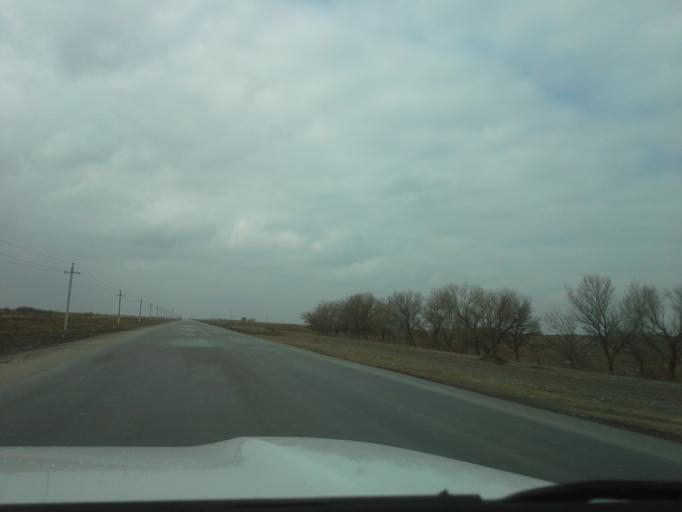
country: TM
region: Ahal
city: Tejen
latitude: 37.2257
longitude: 61.1319
